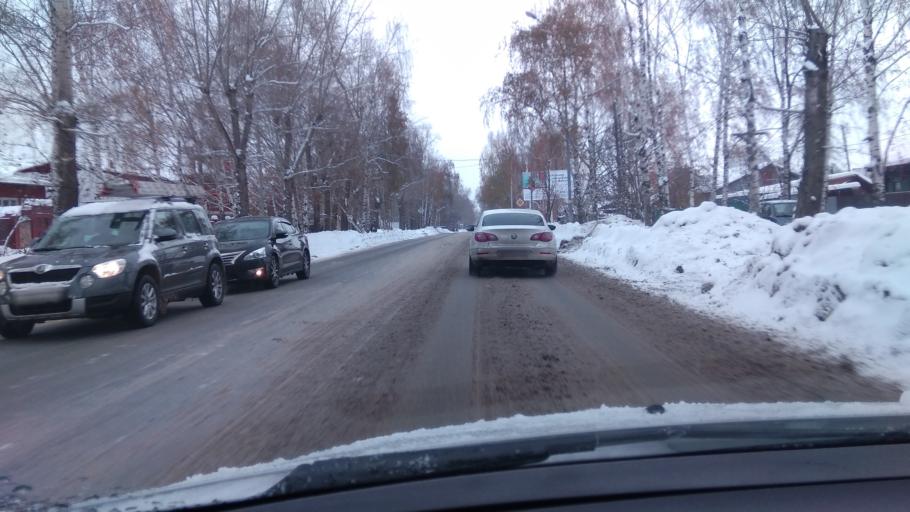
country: RU
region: Sverdlovsk
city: Yekaterinburg
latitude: 56.8070
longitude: 60.5905
